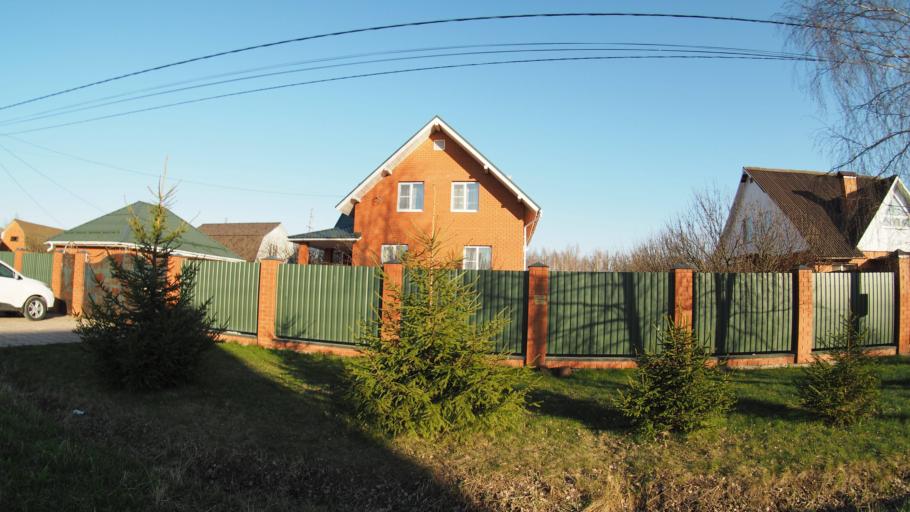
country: RU
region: Moskovskaya
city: Malyshevo
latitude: 55.4888
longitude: 38.3533
